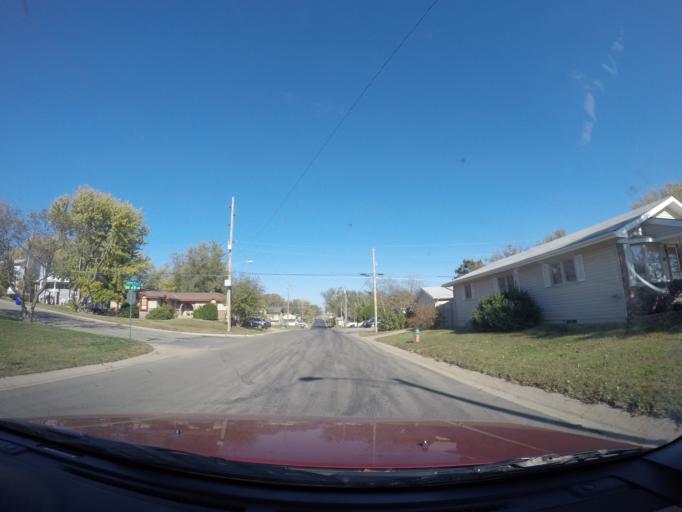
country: US
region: Kansas
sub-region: Geary County
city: Junction City
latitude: 39.0104
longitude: -96.8371
